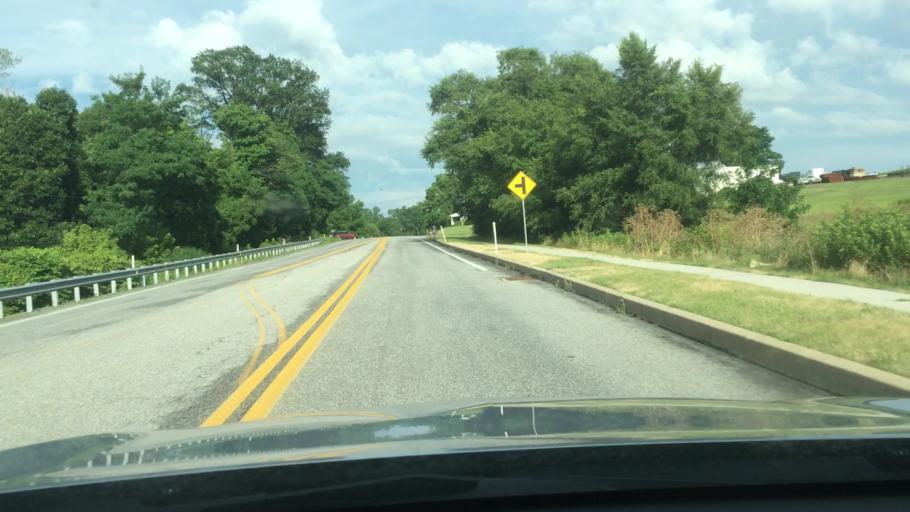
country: US
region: Pennsylvania
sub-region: York County
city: Dillsburg
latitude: 40.1049
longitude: -77.0193
